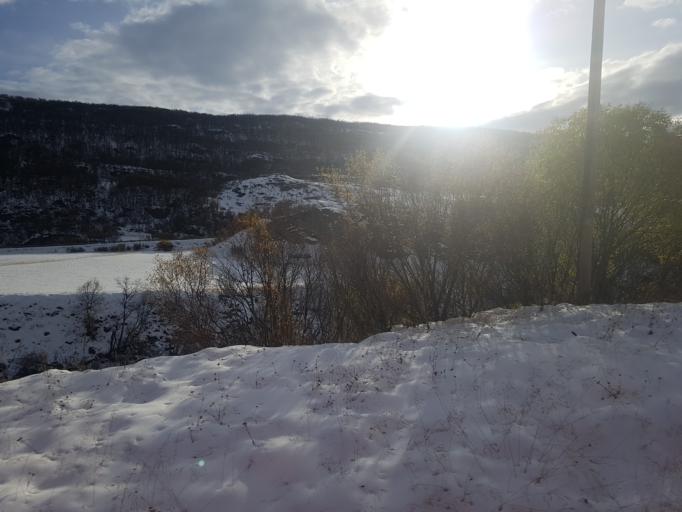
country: NO
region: Sor-Trondelag
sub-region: Oppdal
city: Oppdal
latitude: 62.2993
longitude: 9.6019
